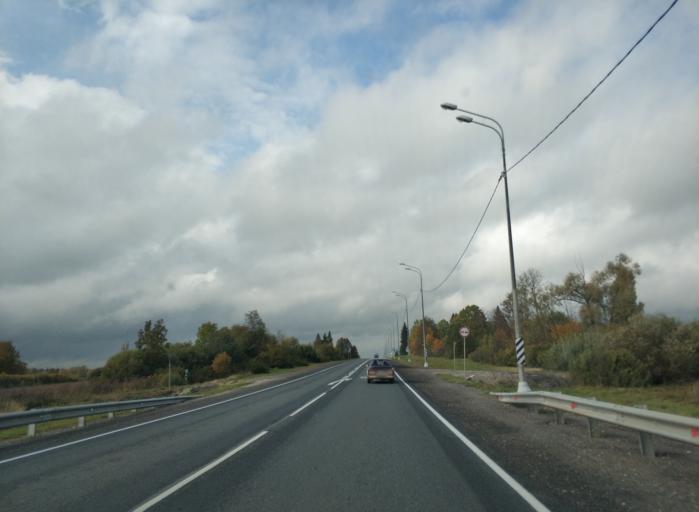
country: RU
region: Pskov
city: Ostrov
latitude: 57.1124
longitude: 28.5338
